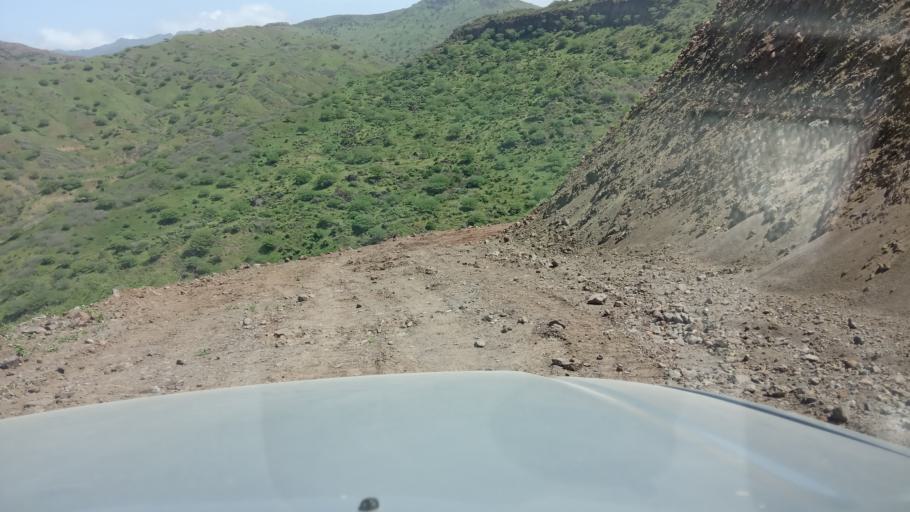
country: CV
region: Santa Catarina
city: Assomada
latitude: 15.1110
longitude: -23.7287
